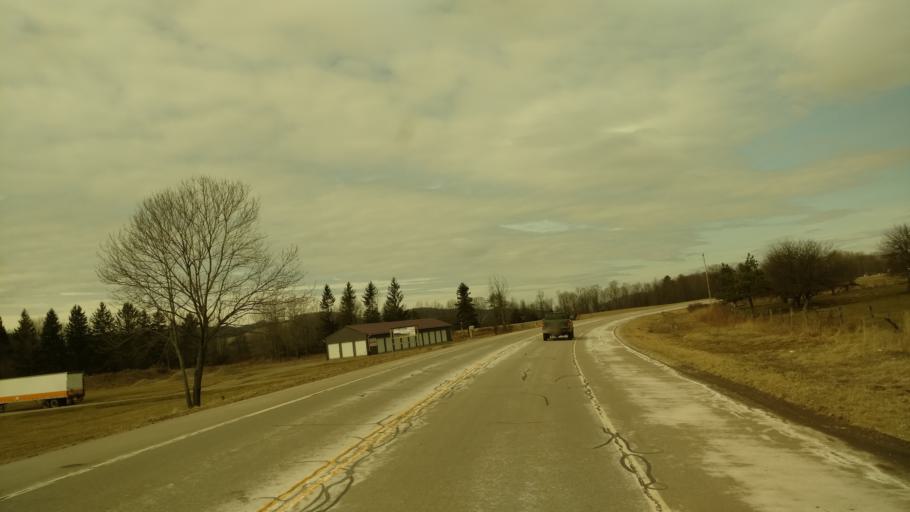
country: US
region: New York
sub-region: Allegany County
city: Wellsville
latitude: 42.0622
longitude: -77.9193
